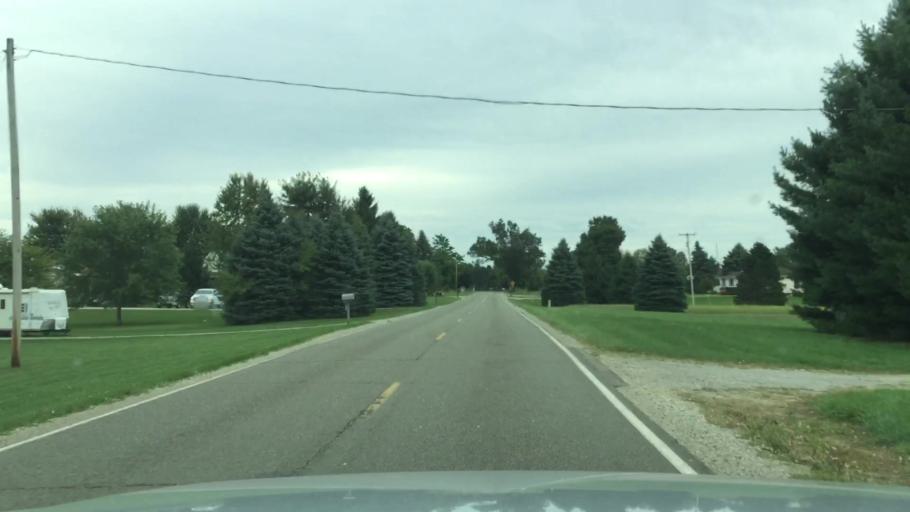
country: US
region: Michigan
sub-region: Shiawassee County
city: Durand
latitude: 42.8332
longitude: -84.0315
